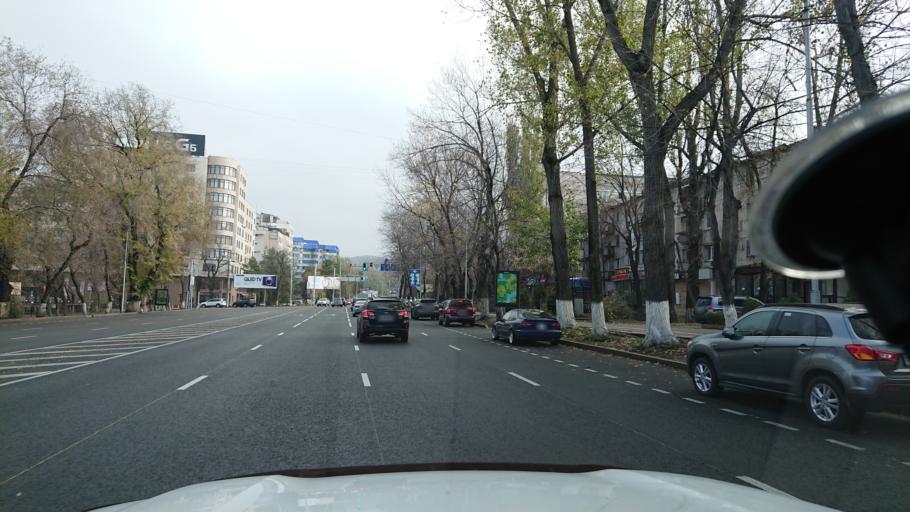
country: KZ
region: Almaty Qalasy
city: Almaty
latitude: 43.2392
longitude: 76.9558
